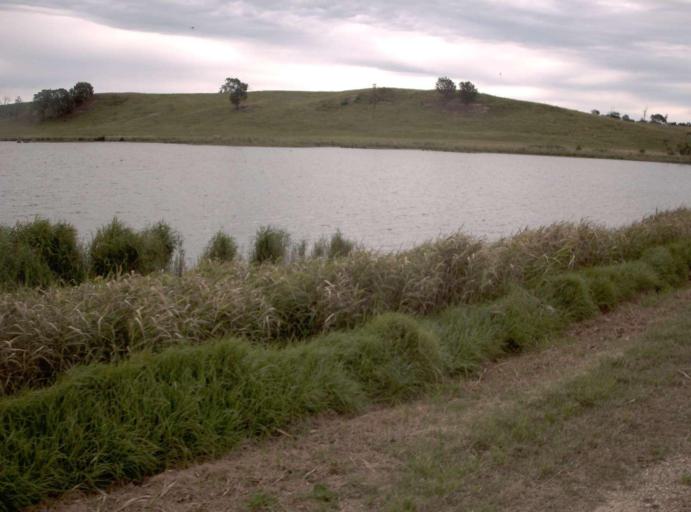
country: AU
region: Victoria
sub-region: Wellington
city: Sale
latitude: -38.0157
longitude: 147.1883
